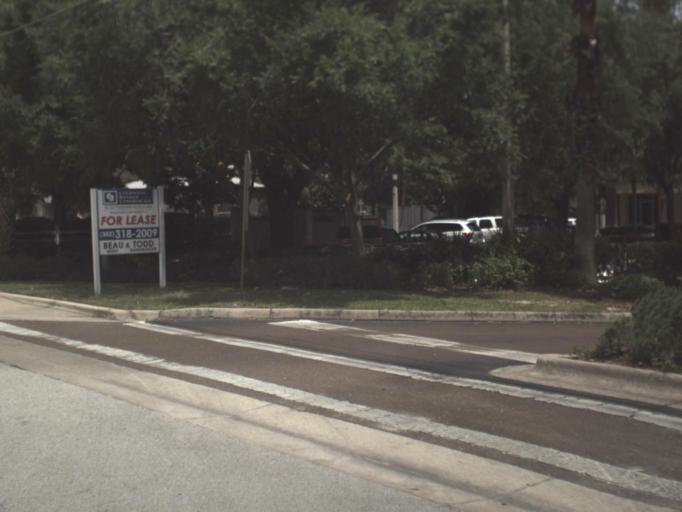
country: US
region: Florida
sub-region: Alachua County
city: Gainesville
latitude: 29.6529
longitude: -82.3822
